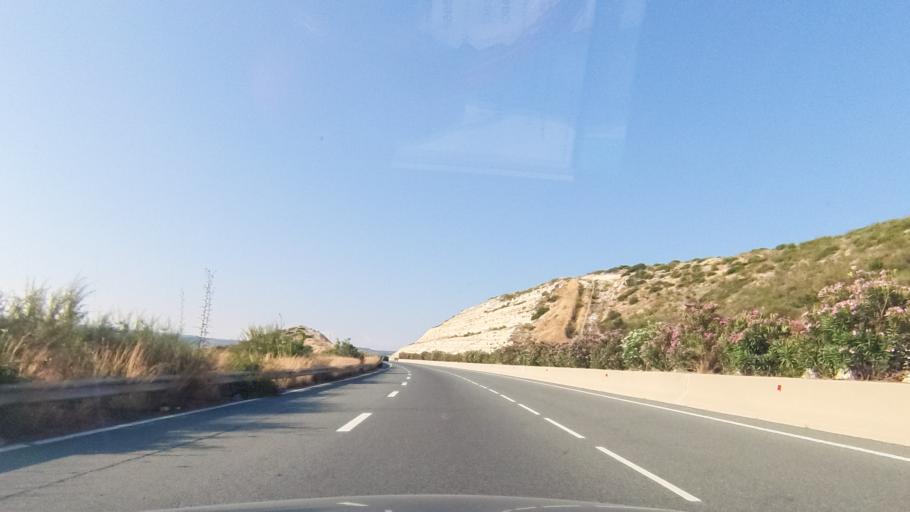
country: CY
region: Limassol
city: Sotira
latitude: 34.6813
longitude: 32.8047
